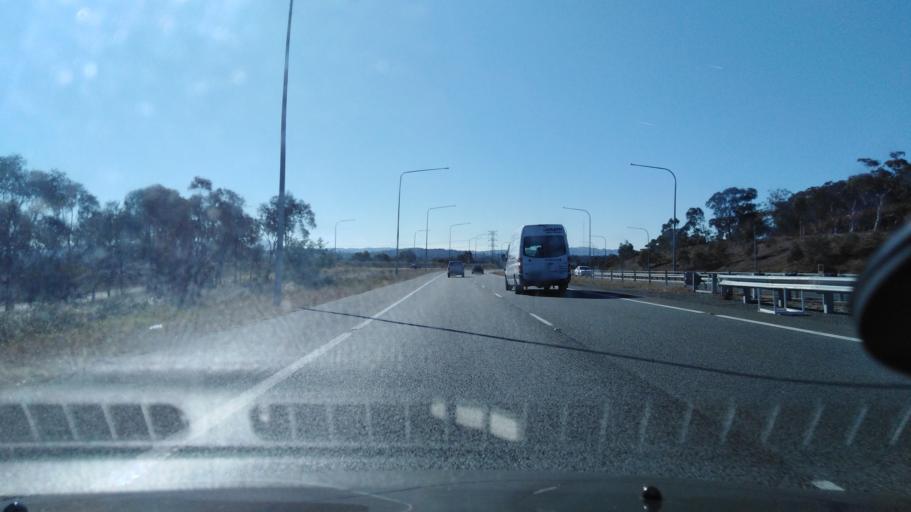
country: AU
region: Australian Capital Territory
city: Kaleen
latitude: -35.2427
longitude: 149.1107
